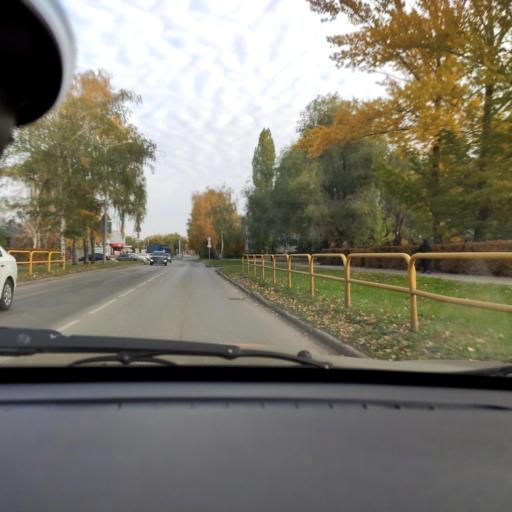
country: RU
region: Samara
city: Tol'yatti
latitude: 53.5121
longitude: 49.2844
